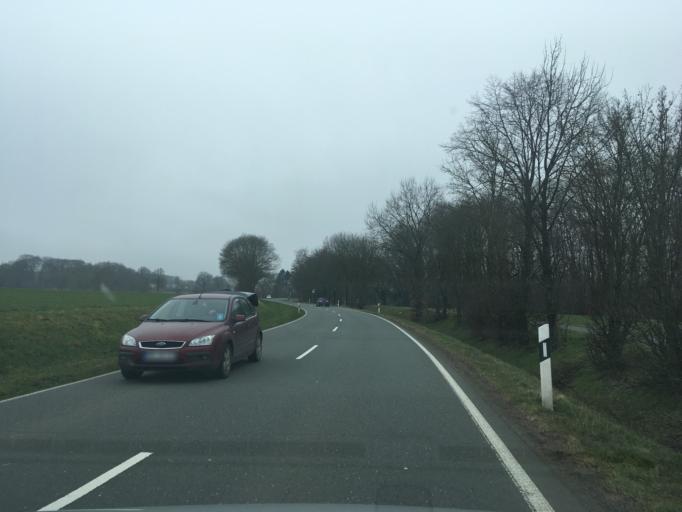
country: DE
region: North Rhine-Westphalia
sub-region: Regierungsbezirk Munster
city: Borken
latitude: 51.8420
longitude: 6.8189
